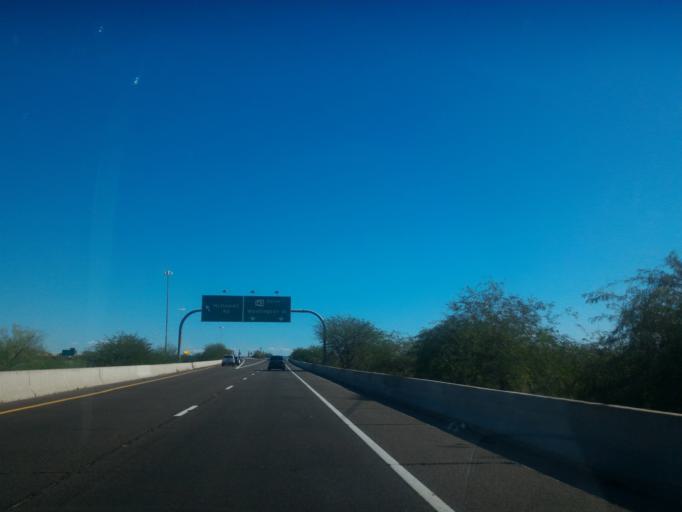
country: US
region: Arizona
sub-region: Maricopa County
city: Tempe Junction
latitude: 33.4581
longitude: -111.9887
